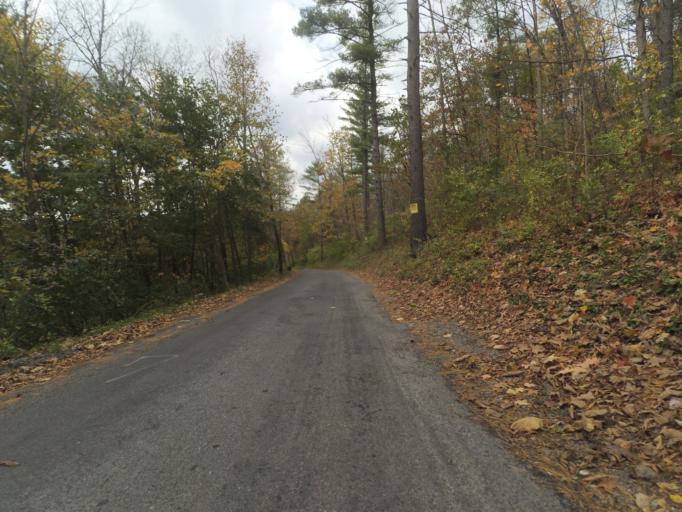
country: US
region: Pennsylvania
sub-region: Centre County
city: Bellefonte
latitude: 40.8877
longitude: -77.7868
